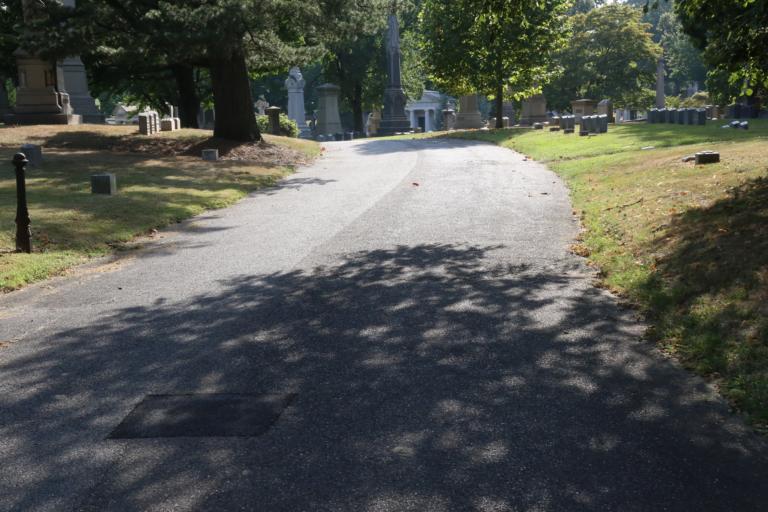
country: US
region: New York
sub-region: Bronx
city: Eastchester
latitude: 40.8912
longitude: -73.8677
